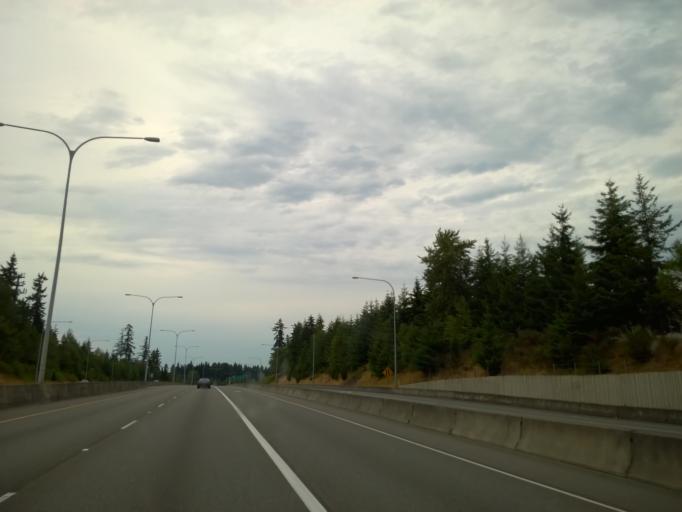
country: US
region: Washington
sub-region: King County
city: Redmond
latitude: 47.6492
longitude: -122.1363
